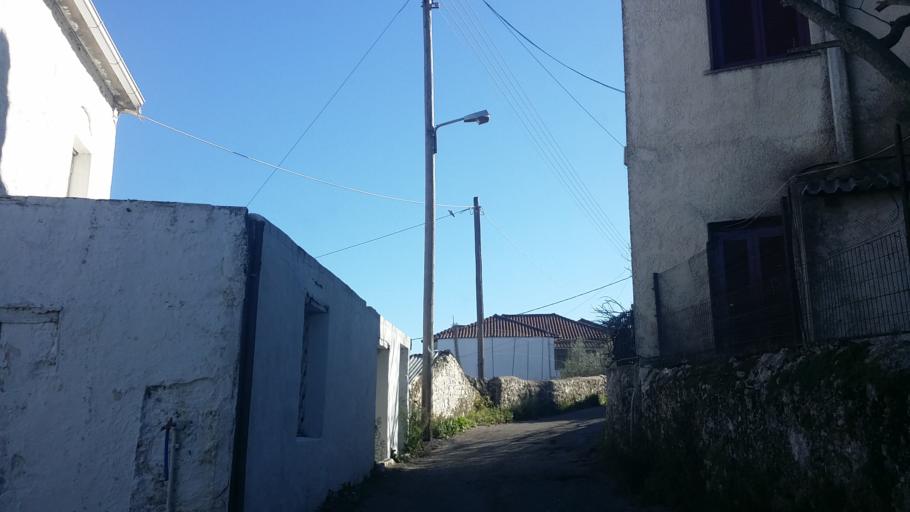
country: GR
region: West Greece
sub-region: Nomos Aitolias kai Akarnanias
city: Fitiai
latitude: 38.7109
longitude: 21.1739
